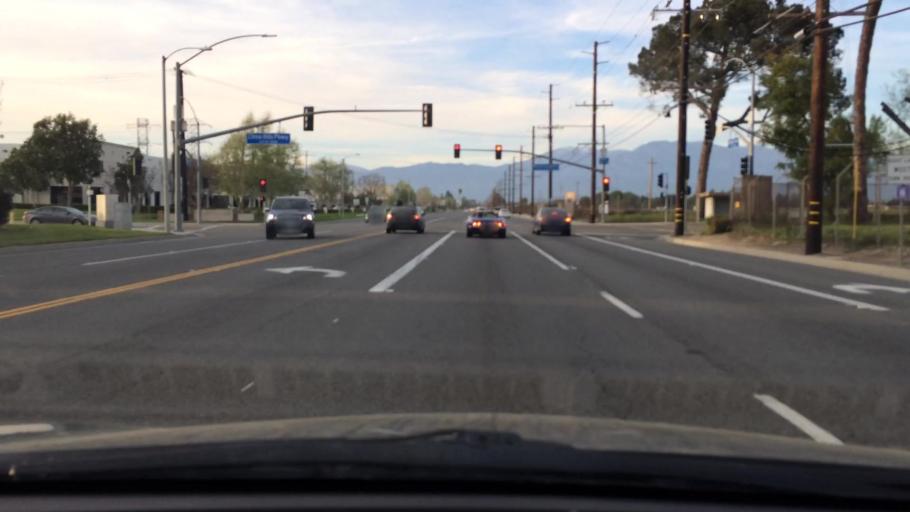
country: US
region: California
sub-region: San Bernardino County
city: Los Serranos
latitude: 33.9823
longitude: -117.6890
